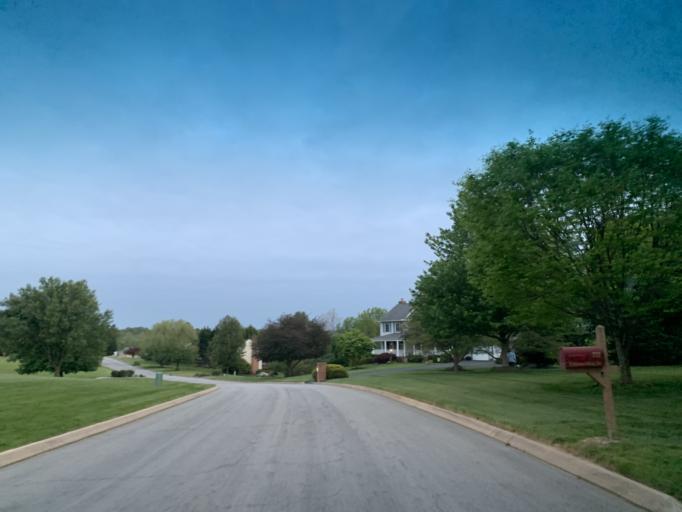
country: US
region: Maryland
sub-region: Harford County
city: South Bel Air
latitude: 39.5934
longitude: -76.2686
